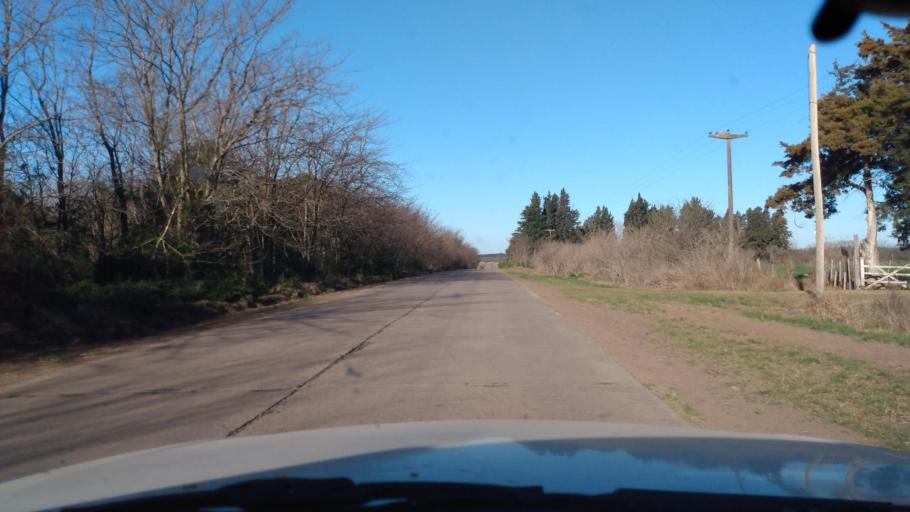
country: AR
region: Buenos Aires
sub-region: Partido de Mercedes
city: Mercedes
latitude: -34.6132
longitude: -59.2787
